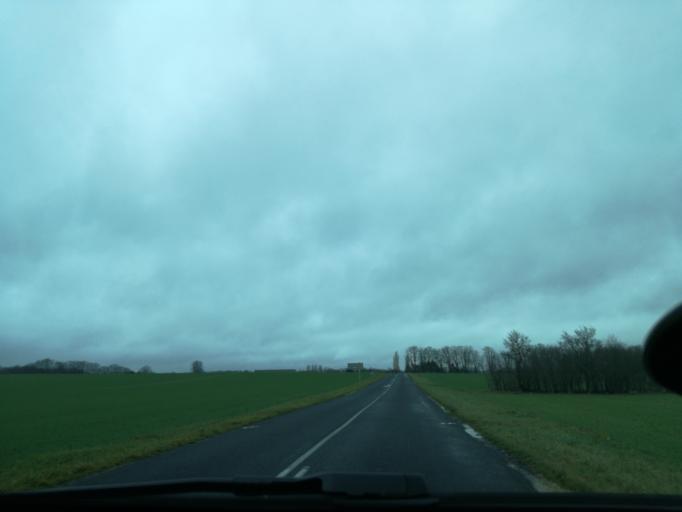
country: FR
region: Lorraine
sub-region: Departement de la Meuse
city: Clermont-en-Argonne
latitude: 49.0539
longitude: 5.1240
